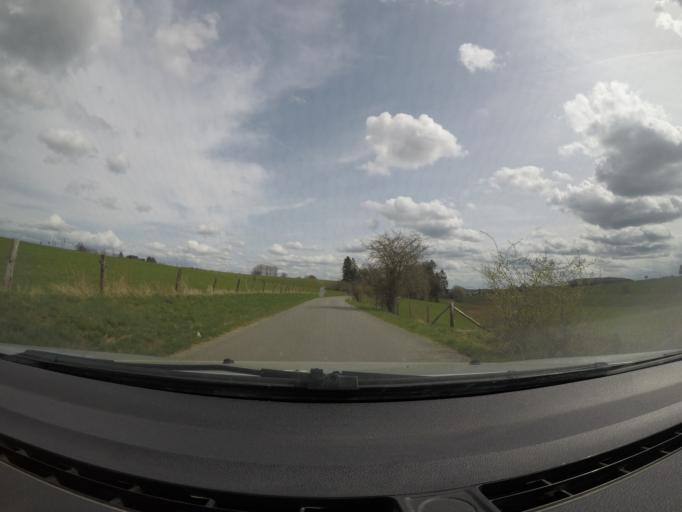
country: BE
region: Wallonia
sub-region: Province du Luxembourg
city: Neufchateau
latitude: 49.8218
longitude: 5.4650
